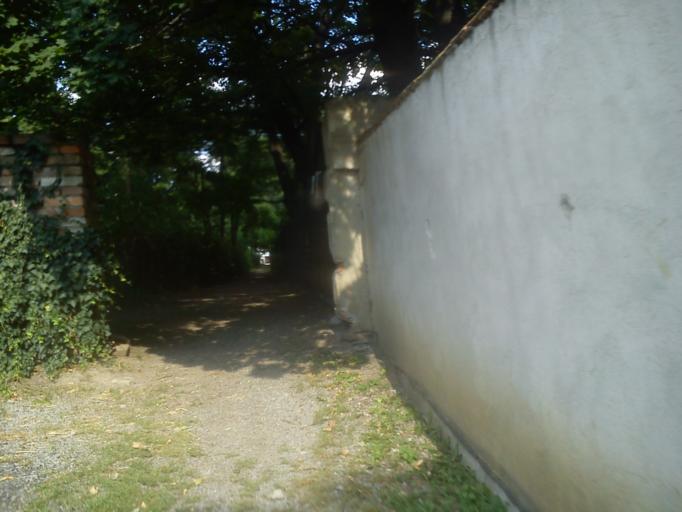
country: CZ
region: South Moravian
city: Sokolnice
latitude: 49.1190
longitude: 16.7253
